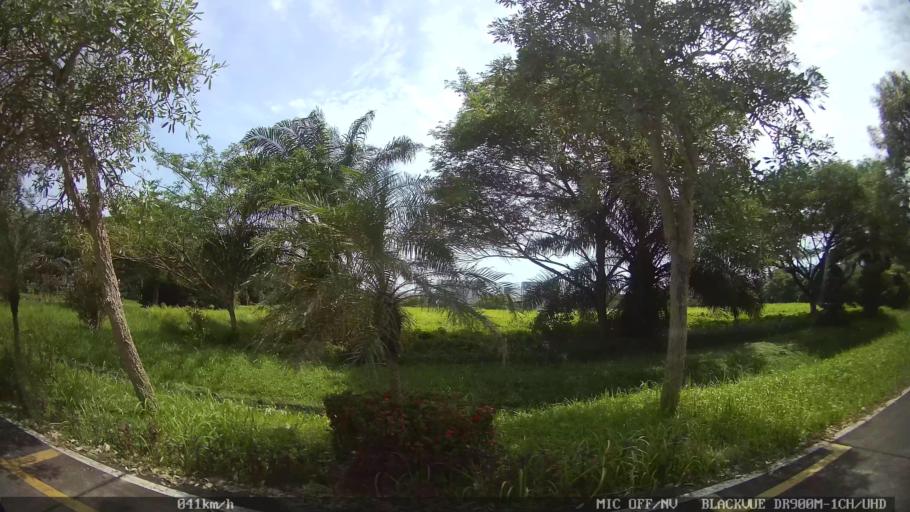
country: ID
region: North Sumatra
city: Percut
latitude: 3.6237
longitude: 98.8662
